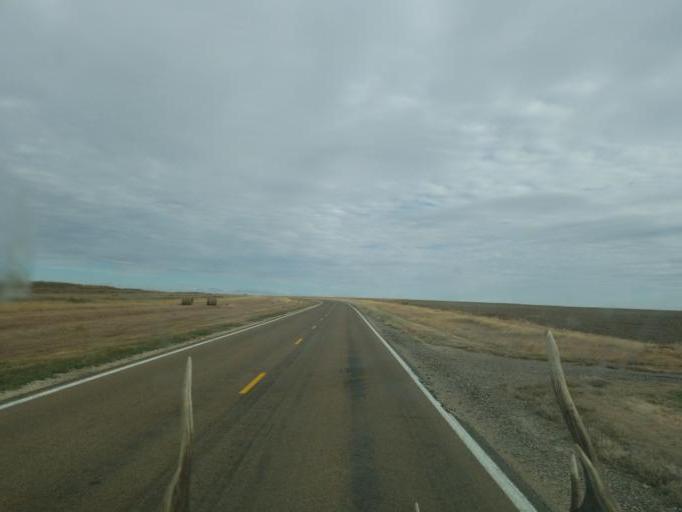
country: US
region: Kansas
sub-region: Thomas County
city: Colby
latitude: 39.0333
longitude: -101.2824
